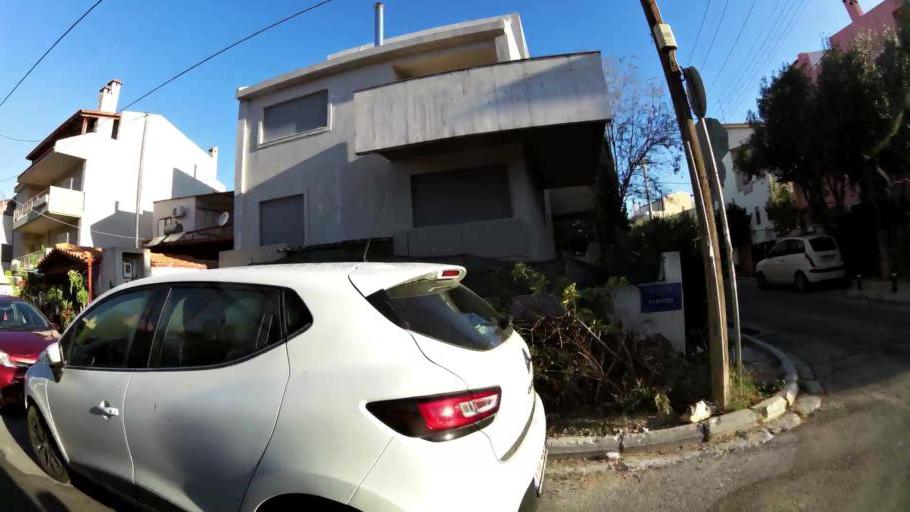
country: GR
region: Attica
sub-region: Nomarchia Athinas
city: Agia Paraskevi
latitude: 38.0257
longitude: 23.8382
